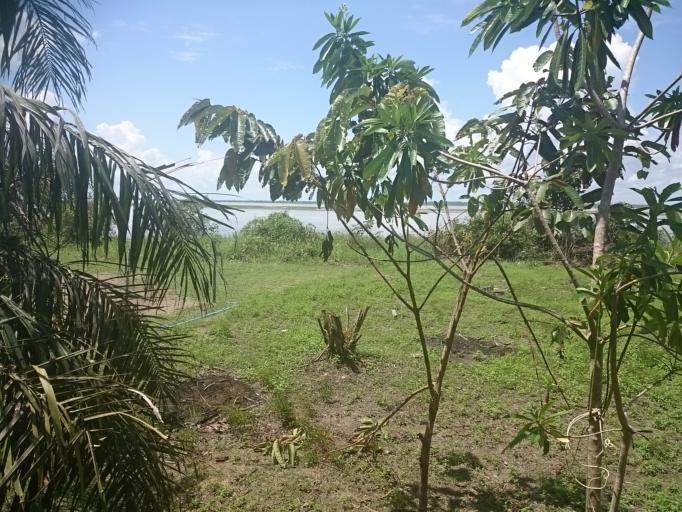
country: PE
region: Loreto
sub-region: Provincia de Maynas
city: Iquitos
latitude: -3.6918
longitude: -73.2506
